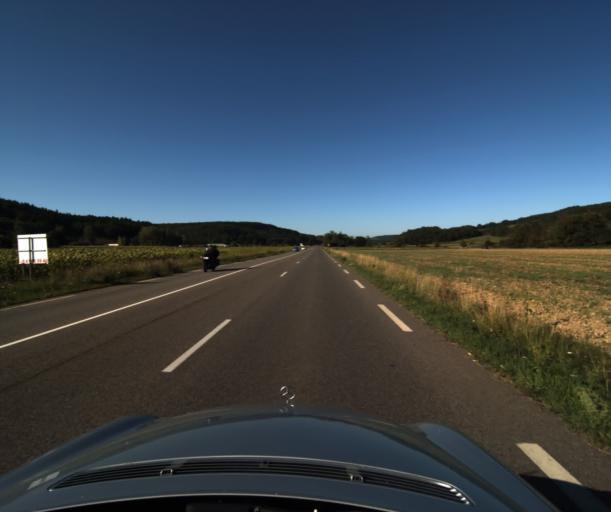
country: FR
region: Midi-Pyrenees
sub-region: Departement de l'Ariege
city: Lavelanet
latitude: 43.0006
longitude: 1.8813
